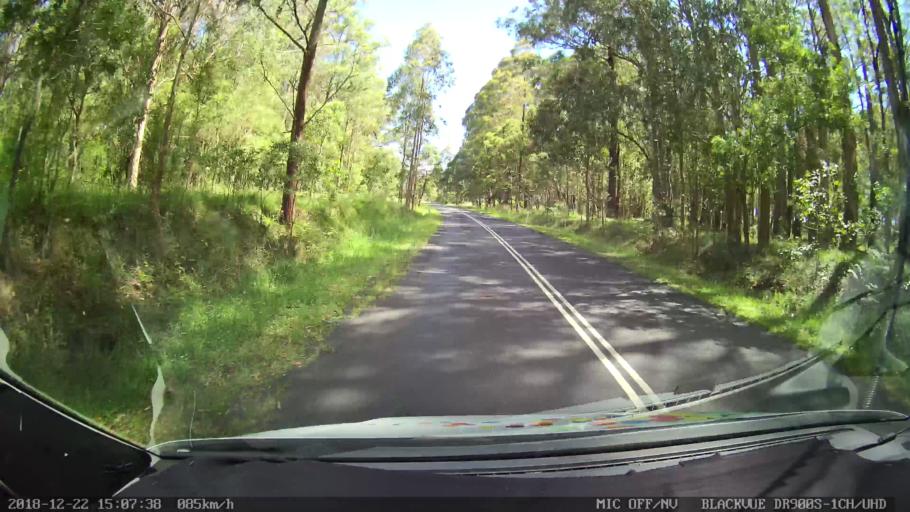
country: AU
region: New South Wales
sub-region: Bellingen
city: Dorrigo
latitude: -30.3019
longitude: 152.4130
